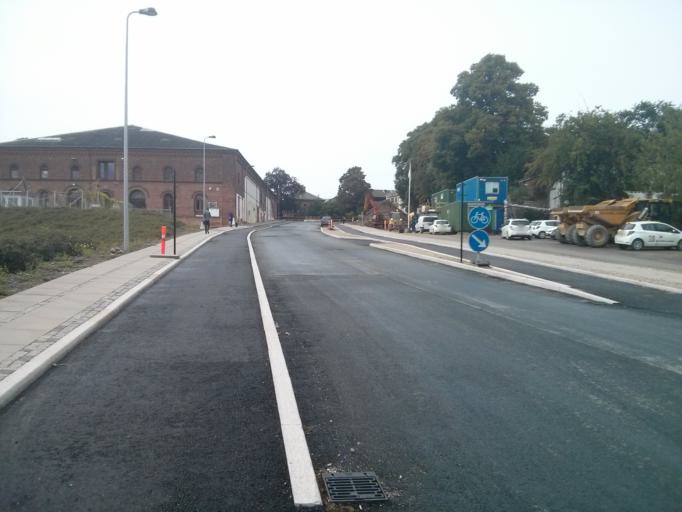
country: DK
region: Capital Region
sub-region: Frederiksberg Kommune
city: Frederiksberg
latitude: 55.6662
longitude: 12.5316
